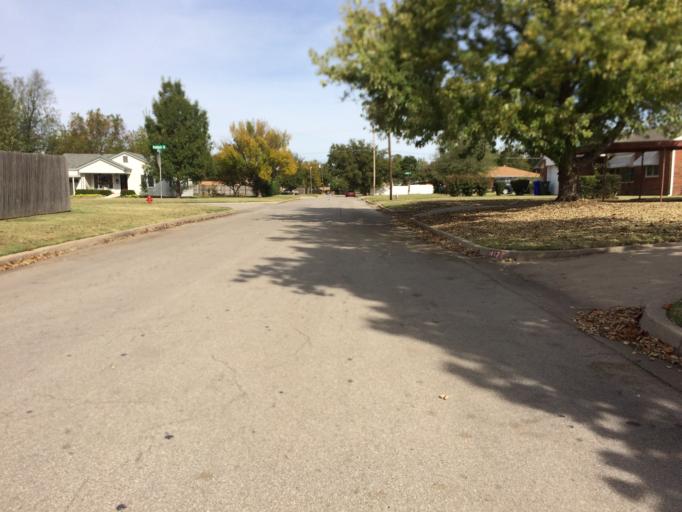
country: US
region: Oklahoma
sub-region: Cleveland County
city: Norman
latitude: 35.2349
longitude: -97.4425
